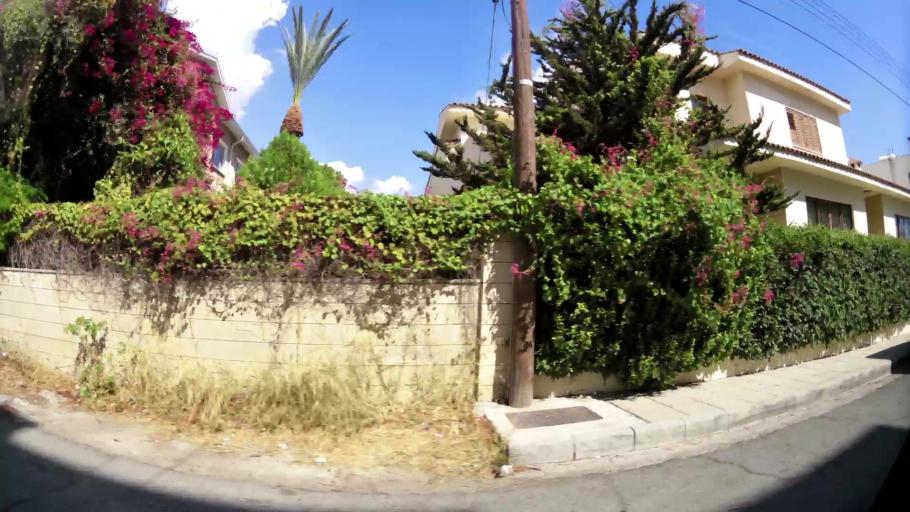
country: CY
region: Larnaka
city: Larnaca
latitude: 34.9160
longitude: 33.6294
